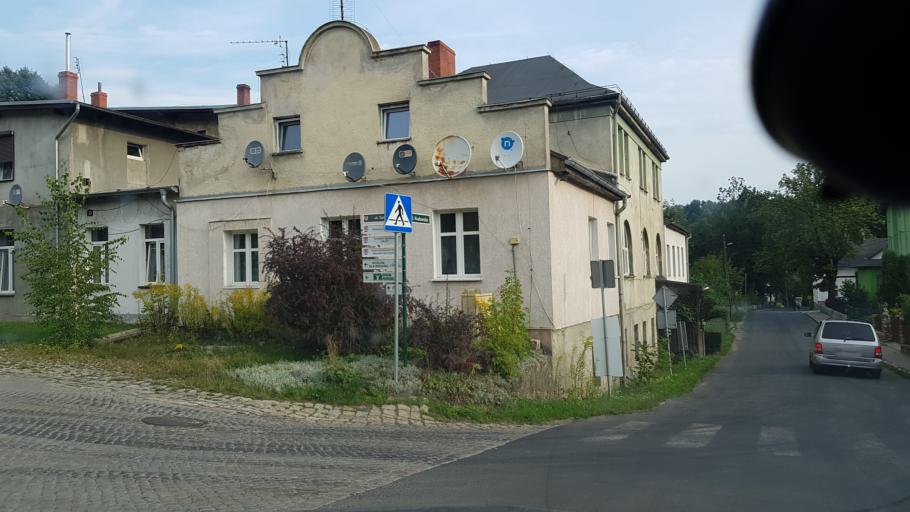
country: PL
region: Lower Silesian Voivodeship
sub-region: Powiat jeleniogorski
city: Janowice Wielkie
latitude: 50.8795
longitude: 15.9235
